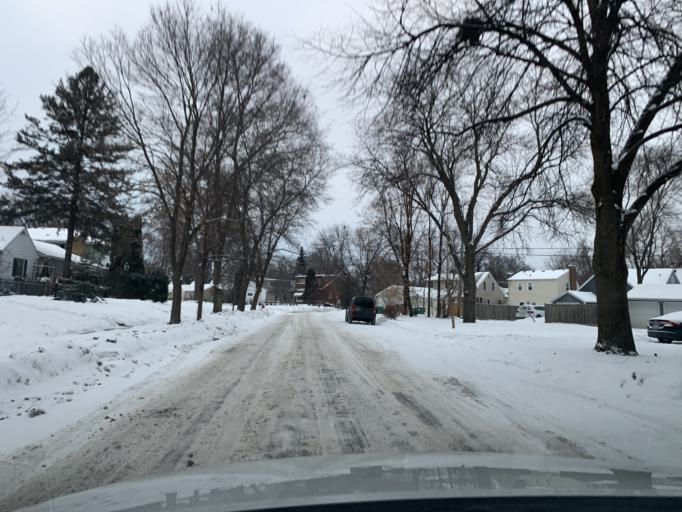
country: US
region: Minnesota
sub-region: Hennepin County
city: Saint Louis Park
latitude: 44.9266
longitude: -93.3457
